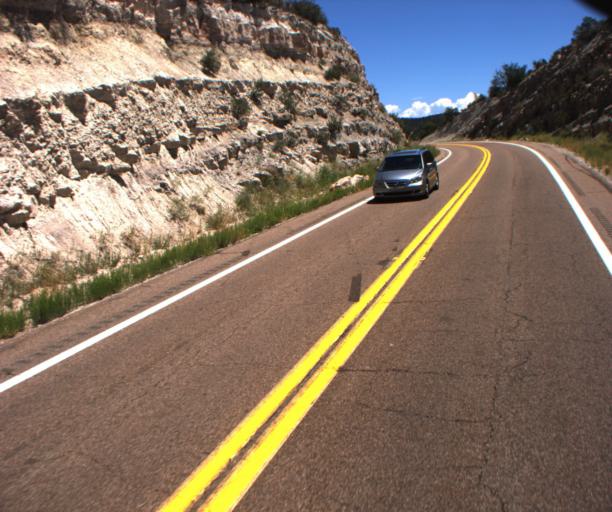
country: US
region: Arizona
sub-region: Navajo County
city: Cibecue
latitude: 33.8326
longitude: -110.4497
